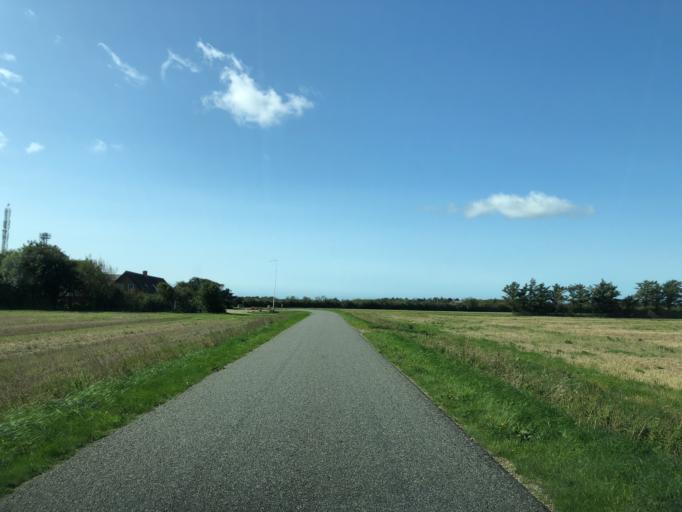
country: DK
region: Central Jutland
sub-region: Holstebro Kommune
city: Ulfborg
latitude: 56.2621
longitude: 8.1734
